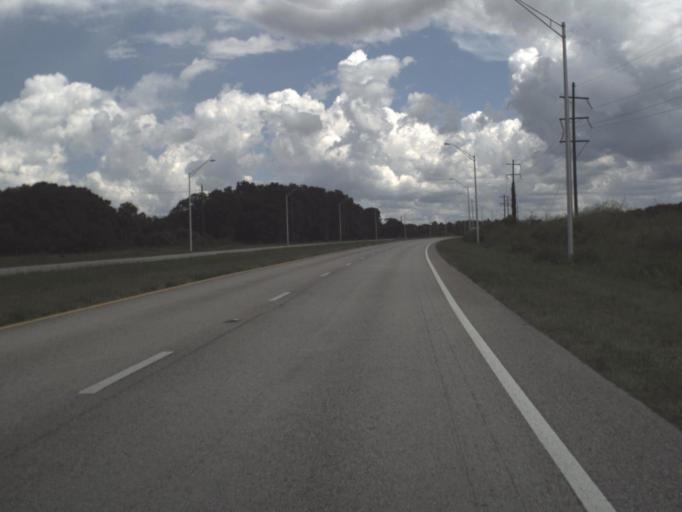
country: US
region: Florida
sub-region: Polk County
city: Babson Park
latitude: 27.8723
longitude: -81.3935
